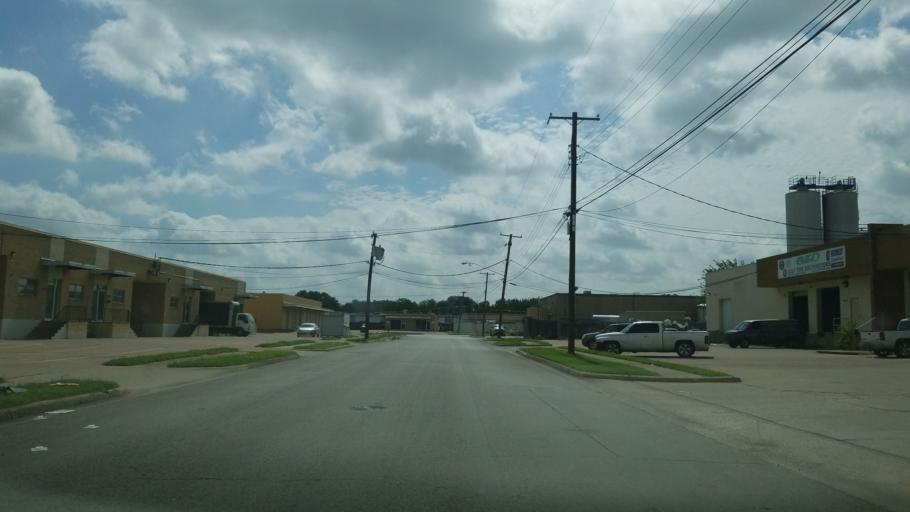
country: US
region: Texas
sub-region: Dallas County
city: Farmers Branch
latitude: 32.8793
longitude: -96.8797
